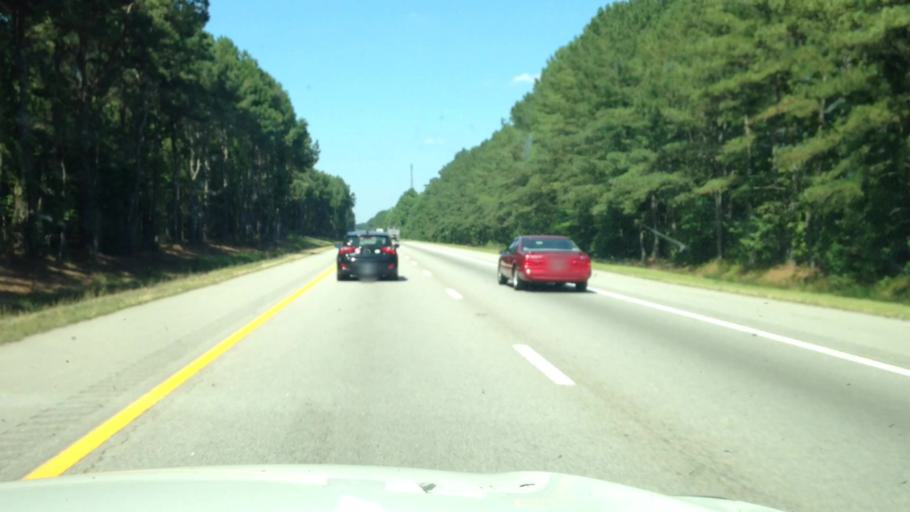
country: US
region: North Carolina
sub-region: Wilson County
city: Lucama
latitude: 35.6710
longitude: -78.0765
